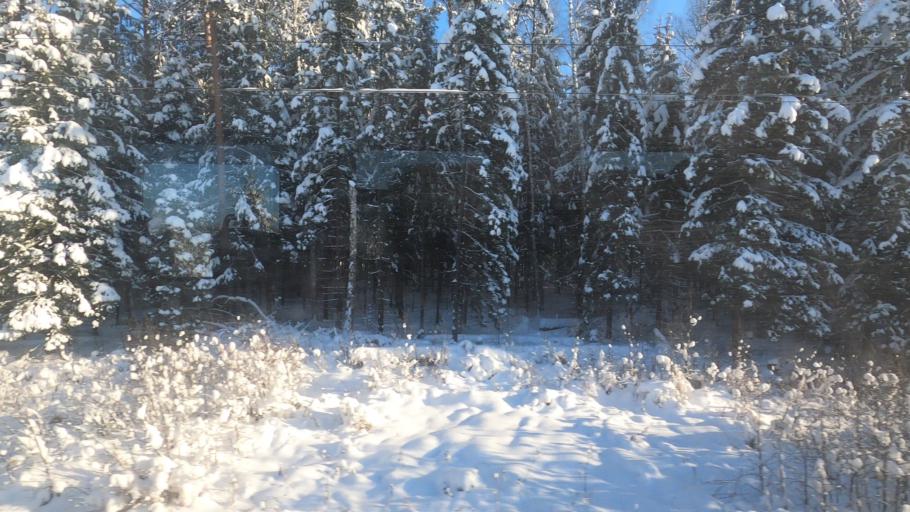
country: RU
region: Moskovskaya
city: Verbilki
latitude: 56.5198
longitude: 37.5572
